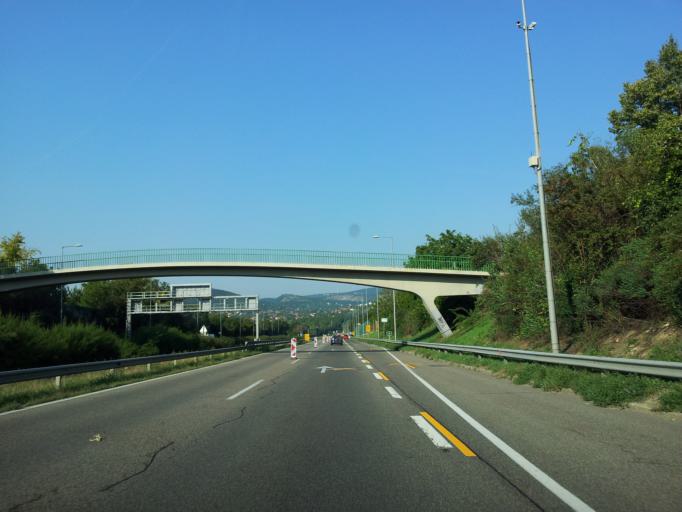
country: HU
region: Pest
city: Toeroekbalint
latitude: 47.4426
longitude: 18.9061
